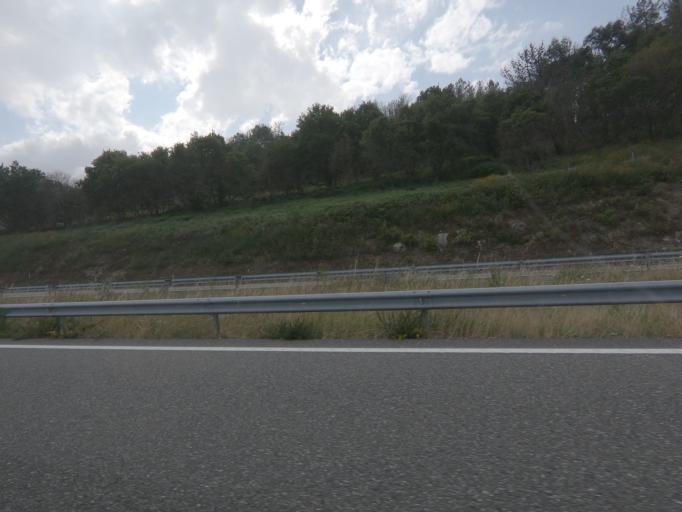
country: ES
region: Galicia
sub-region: Provincia de Ourense
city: Melon
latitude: 42.2524
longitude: -8.2237
